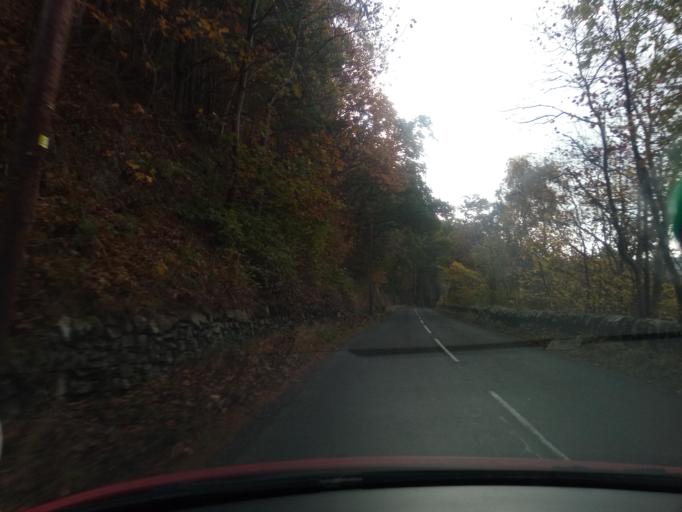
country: GB
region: Scotland
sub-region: The Scottish Borders
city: Selkirk
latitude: 55.5998
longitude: -2.8670
